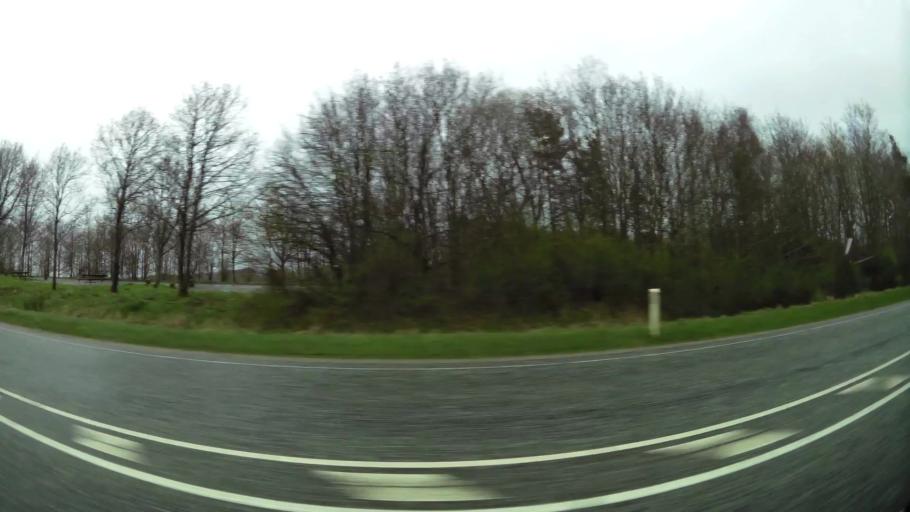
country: DK
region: Central Jutland
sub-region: Herning Kommune
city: Avlum
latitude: 56.2838
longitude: 8.7471
